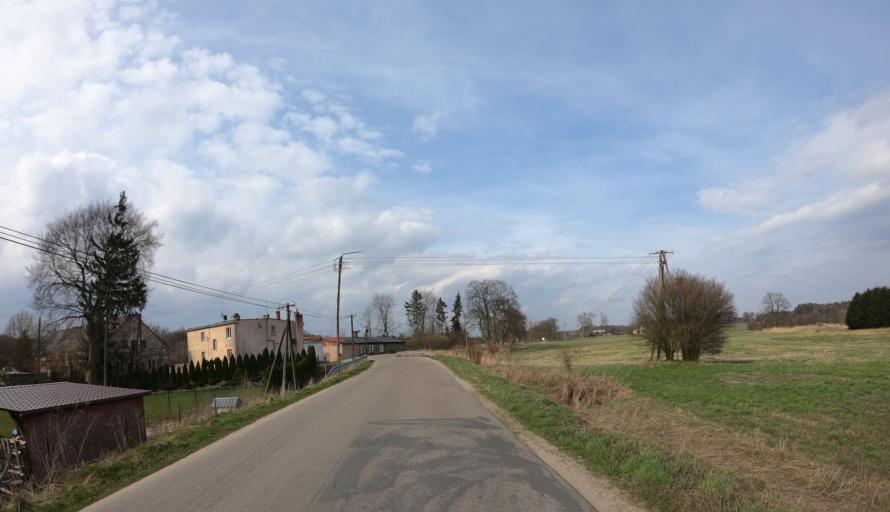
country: PL
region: West Pomeranian Voivodeship
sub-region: Powiat swidwinski
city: Swidwin
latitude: 53.8123
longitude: 15.7940
